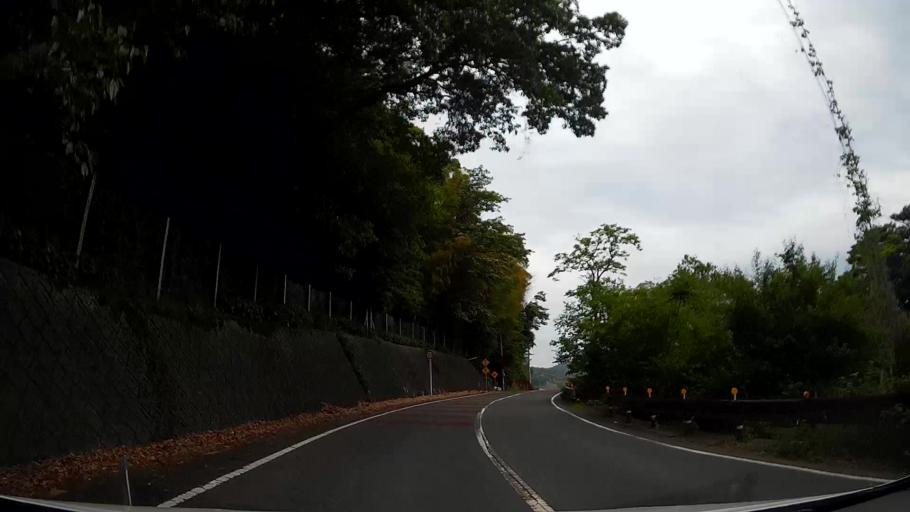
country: JP
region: Shizuoka
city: Ito
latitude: 34.9317
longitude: 138.9359
